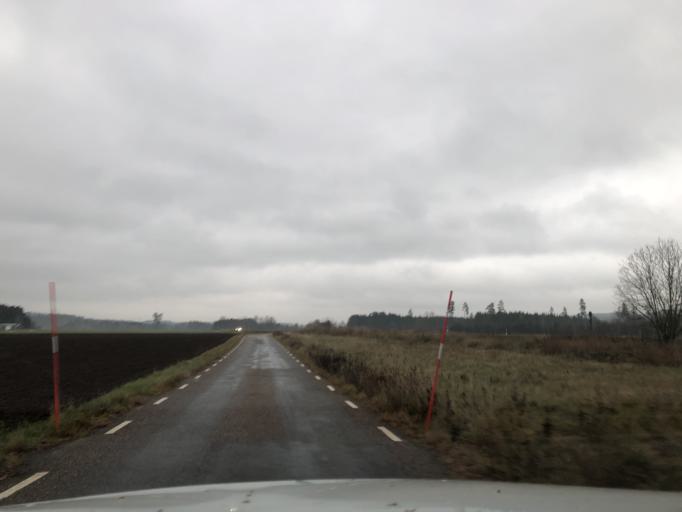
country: SE
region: Vaestra Goetaland
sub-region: Ulricehamns Kommun
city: Ulricehamn
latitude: 57.8693
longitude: 13.4303
